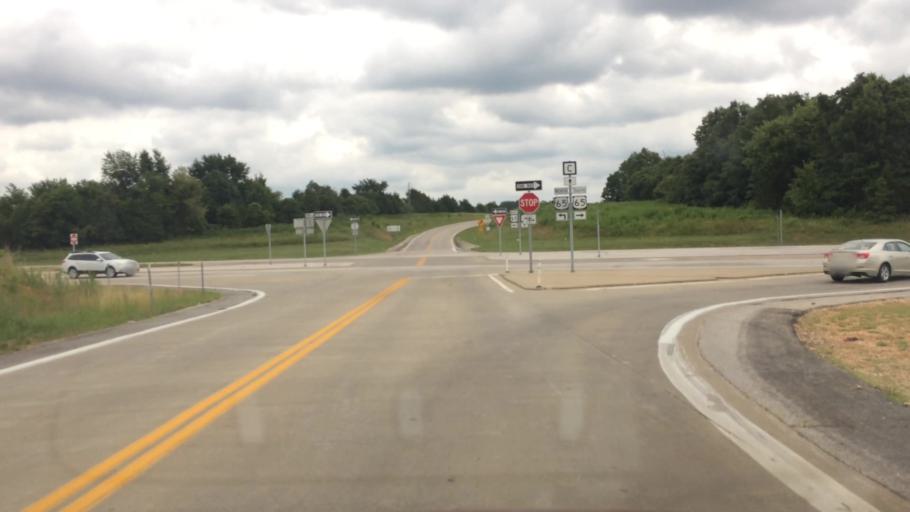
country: US
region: Missouri
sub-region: Greene County
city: Strafford
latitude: 37.3010
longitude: -93.1777
